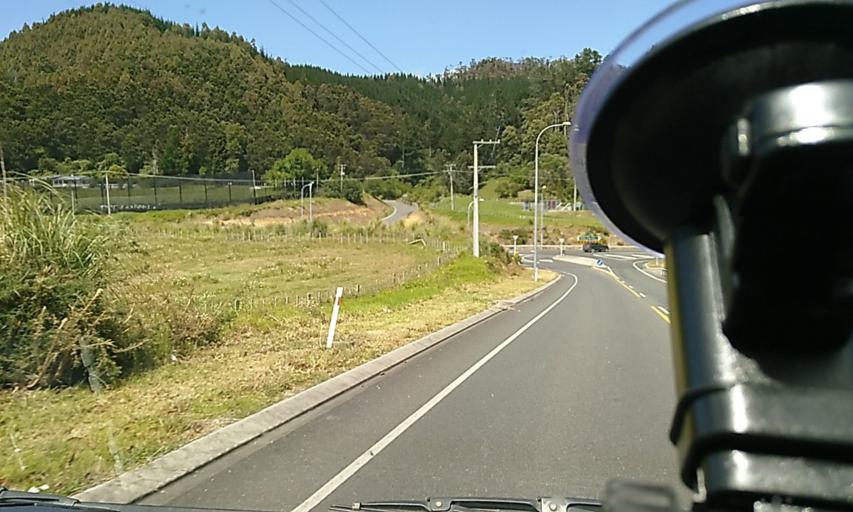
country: NZ
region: Bay of Plenty
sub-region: Western Bay of Plenty District
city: Waihi Beach
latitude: -37.4587
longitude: 175.9310
